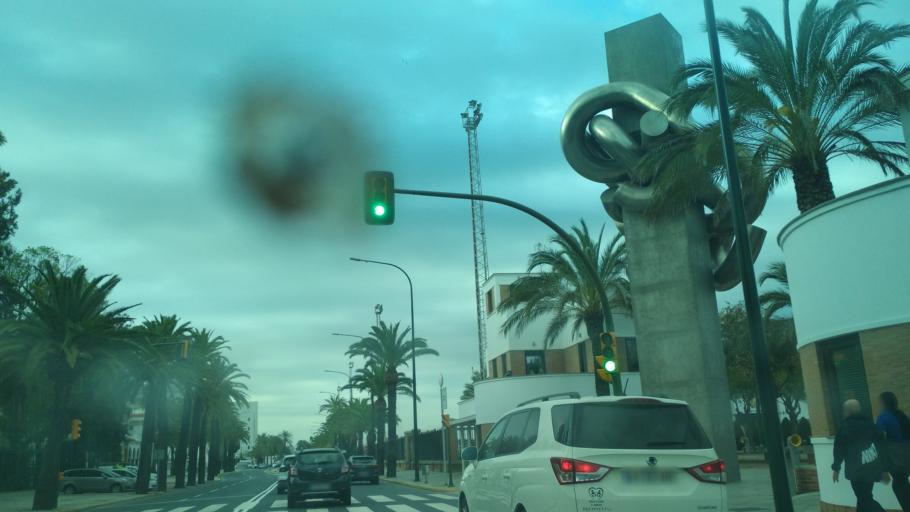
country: ES
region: Andalusia
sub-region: Provincia de Huelva
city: Huelva
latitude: 37.2555
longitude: -6.9594
